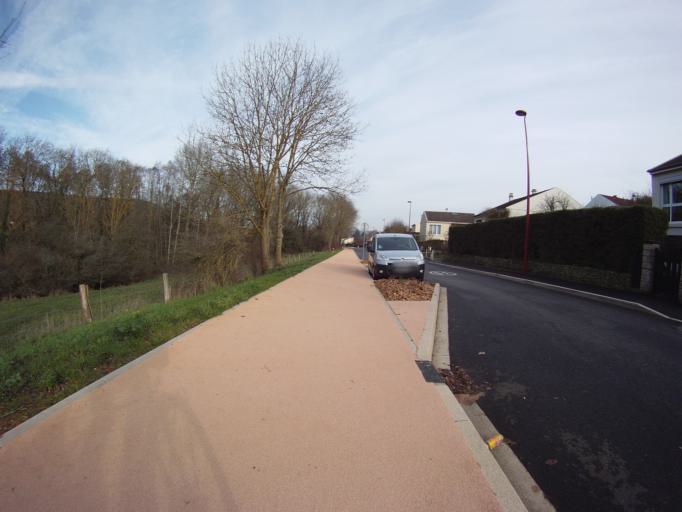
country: FR
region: Lorraine
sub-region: Departement de Meurthe-et-Moselle
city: Champigneulles
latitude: 48.7250
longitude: 6.1531
